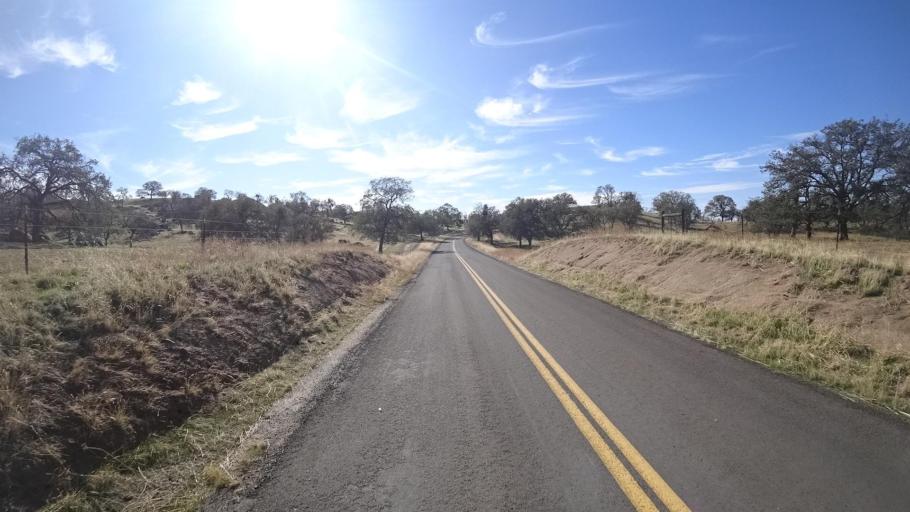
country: US
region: California
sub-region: Kern County
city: Oildale
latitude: 35.6285
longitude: -118.8443
